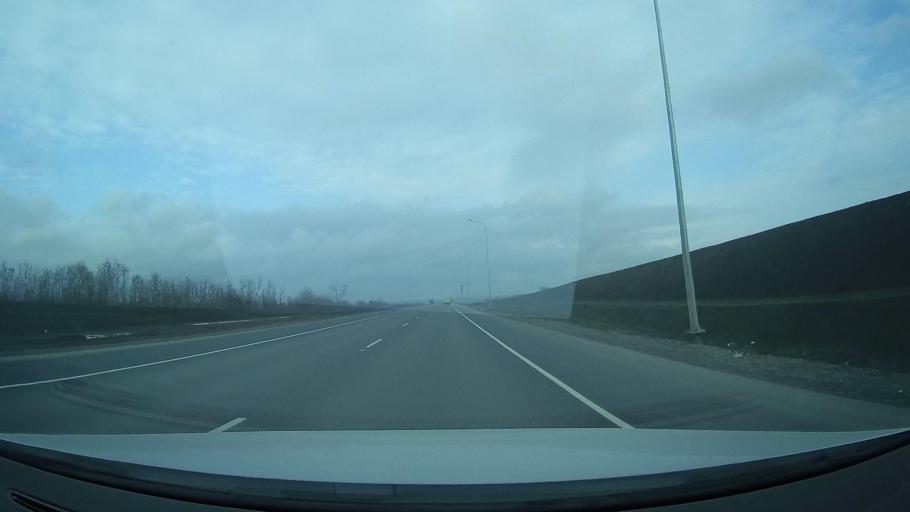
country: RU
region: Rostov
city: Grushevskaya
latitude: 47.4232
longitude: 39.8640
